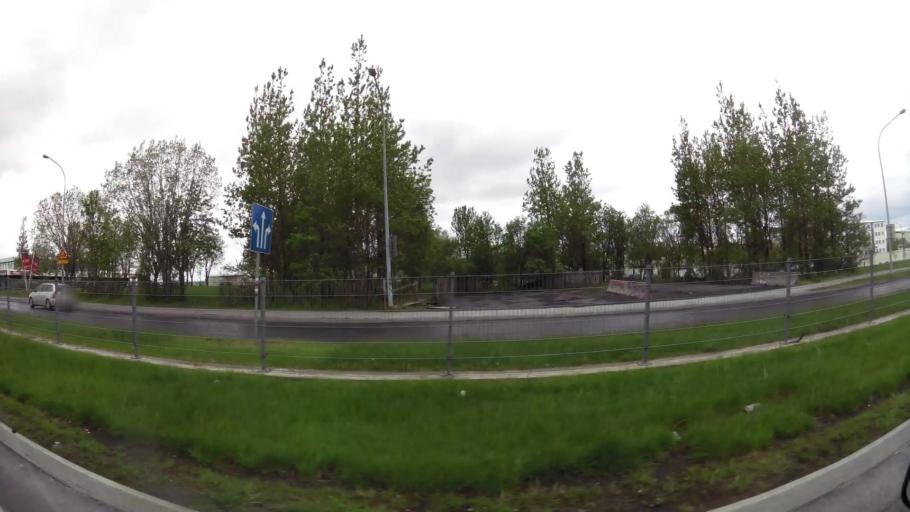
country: IS
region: Capital Region
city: Reykjavik
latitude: 64.1293
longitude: -21.8851
